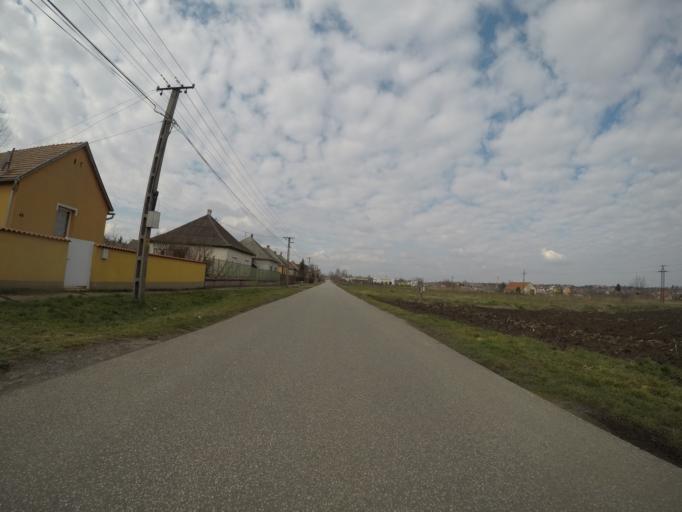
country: HU
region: Tolna
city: Dunafoldvar
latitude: 46.8061
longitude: 18.9132
